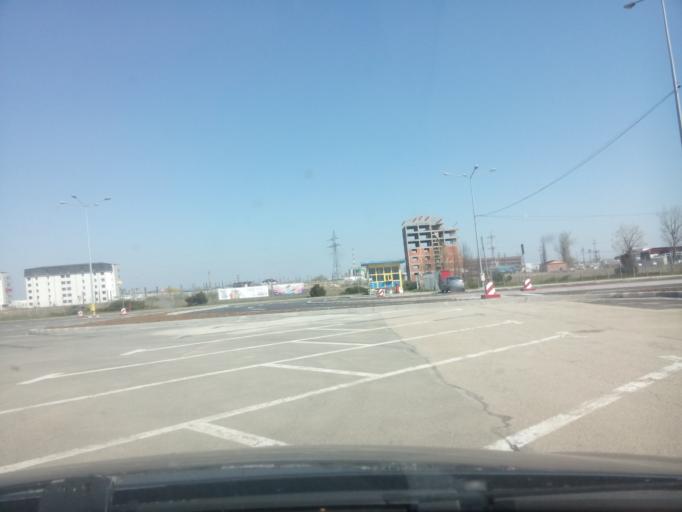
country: RO
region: Ilfov
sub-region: Comuna Pantelimon
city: Pantelimon
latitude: 44.4514
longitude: 26.2220
